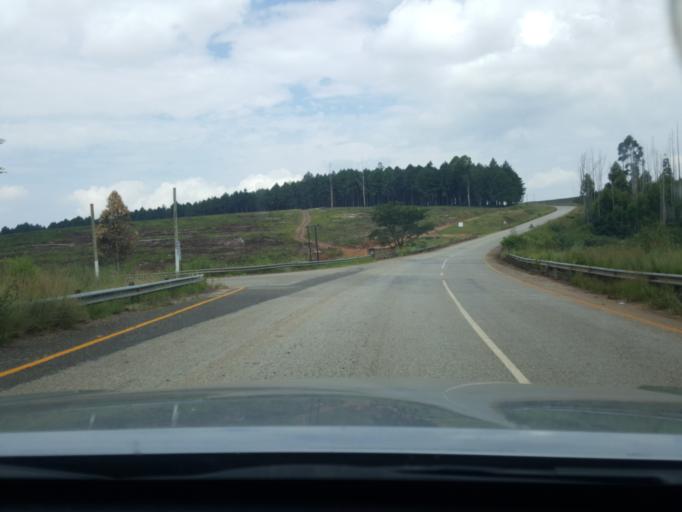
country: ZA
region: Mpumalanga
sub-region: Ehlanzeni District
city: White River
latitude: -25.1946
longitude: 30.9246
